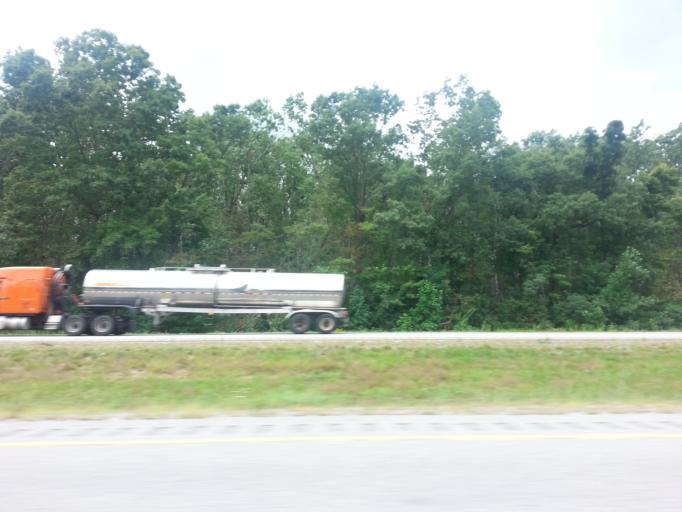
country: US
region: Tennessee
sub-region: Putnam County
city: Monterey
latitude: 36.1264
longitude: -85.2557
